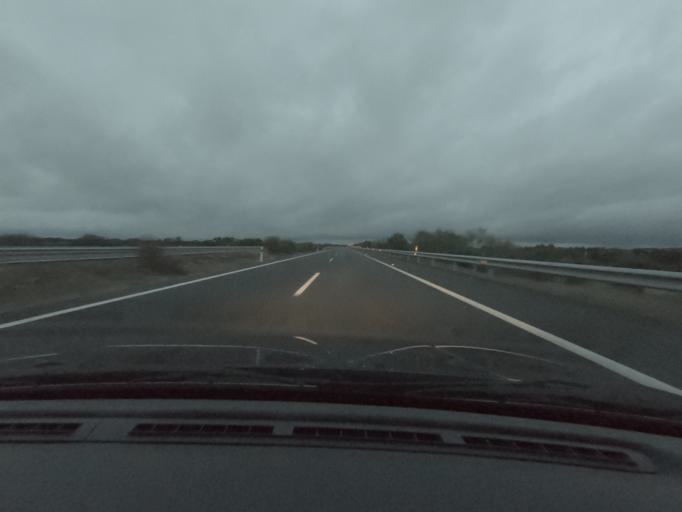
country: ES
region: Extremadura
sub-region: Provincia de Caceres
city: Aldea del Cano
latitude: 39.2613
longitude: -6.3148
